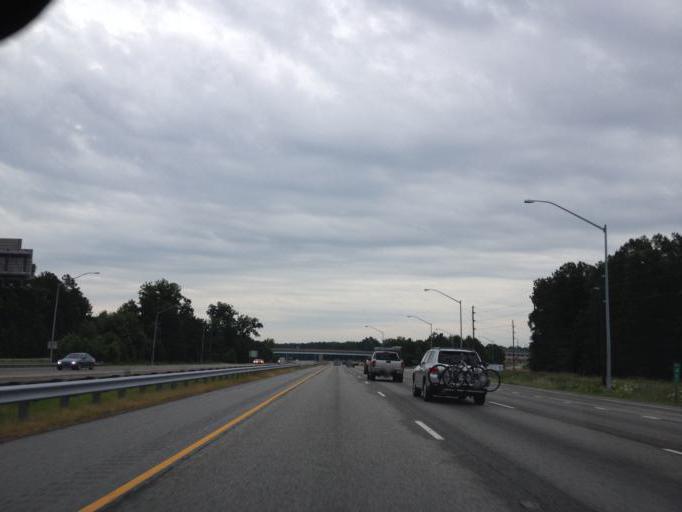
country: US
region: Maryland
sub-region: Queen Anne's County
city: Grasonville
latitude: 38.9666
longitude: -76.1888
